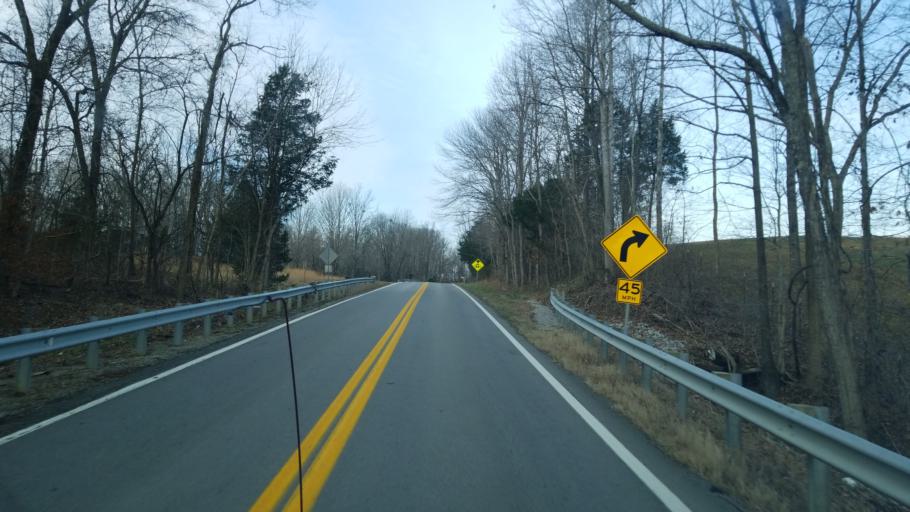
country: US
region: Kentucky
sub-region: Clinton County
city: Albany
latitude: 36.8264
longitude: -85.1957
